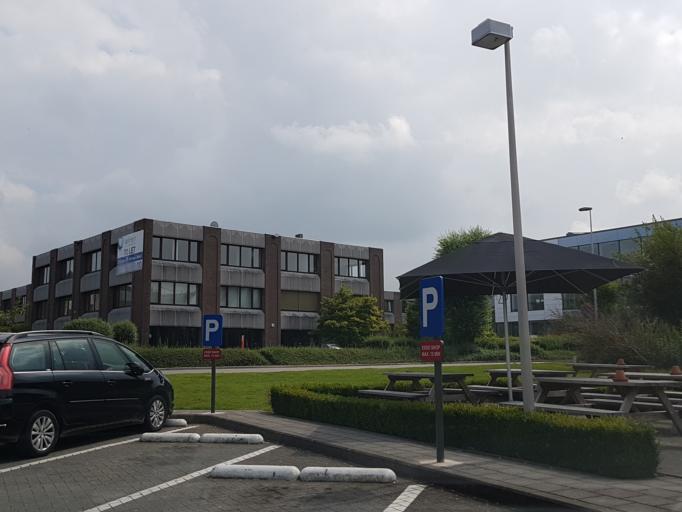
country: BE
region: Flanders
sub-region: Provincie Vlaams-Brabant
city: Zaventem
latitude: 50.8808
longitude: 4.4500
